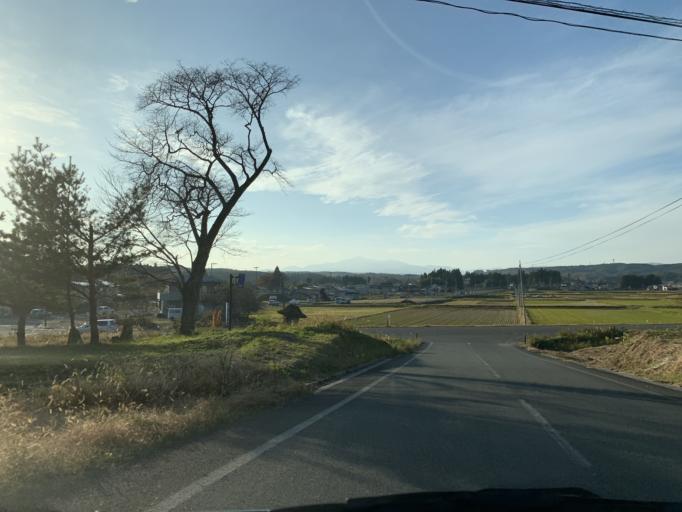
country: JP
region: Iwate
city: Ichinoseki
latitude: 38.9413
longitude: 141.0642
